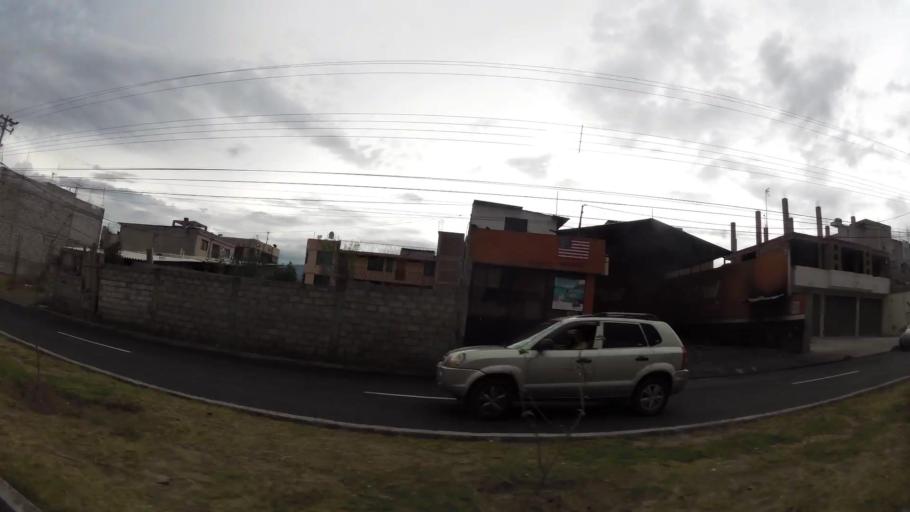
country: EC
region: Tungurahua
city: Ambato
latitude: -1.2753
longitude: -78.6204
